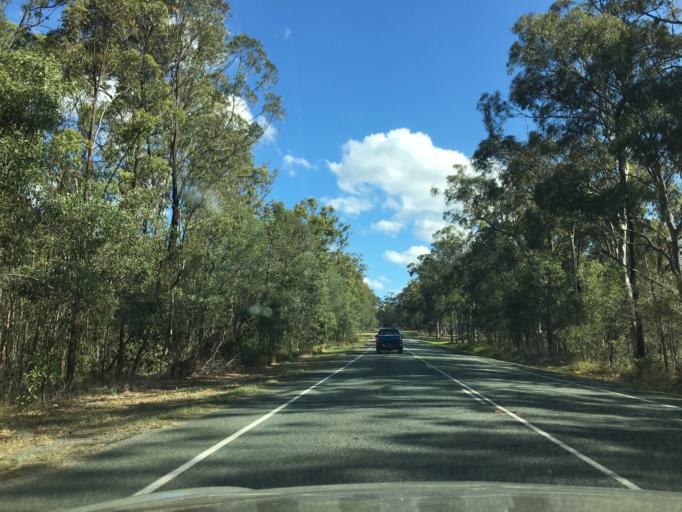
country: AU
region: Queensland
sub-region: Logan
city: Chambers Flat
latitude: -27.7894
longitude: 153.1003
